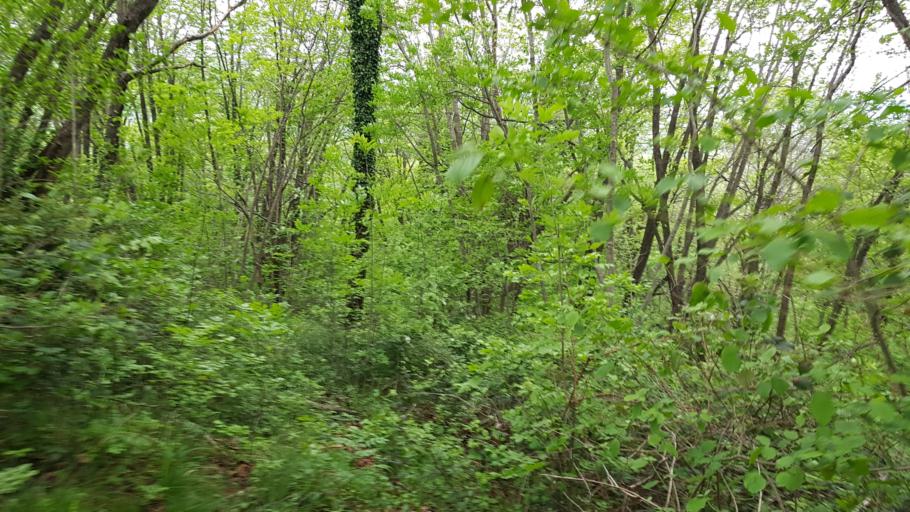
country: IT
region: Friuli Venezia Giulia
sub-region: Provincia di Udine
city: Faedis
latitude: 46.1790
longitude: 13.3567
